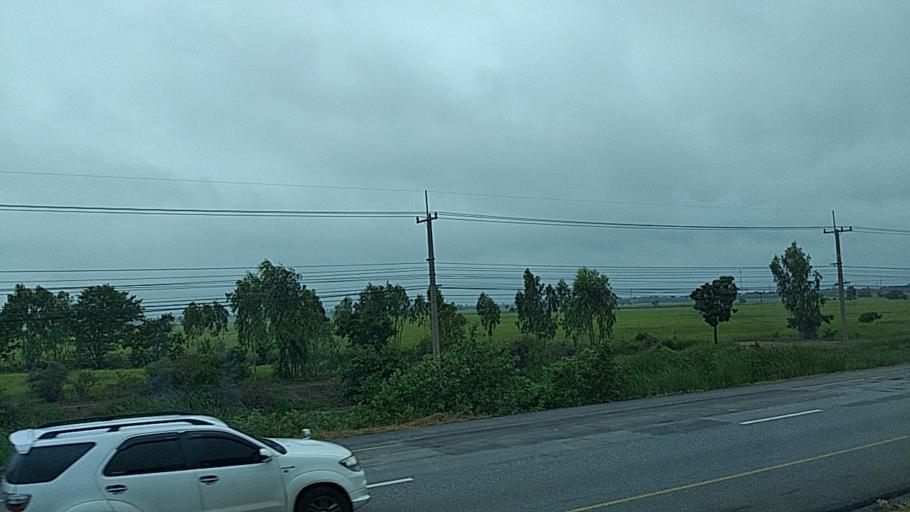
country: TH
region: Nakhon Ratchasima
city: Phimai
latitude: 15.3284
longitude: 102.4377
